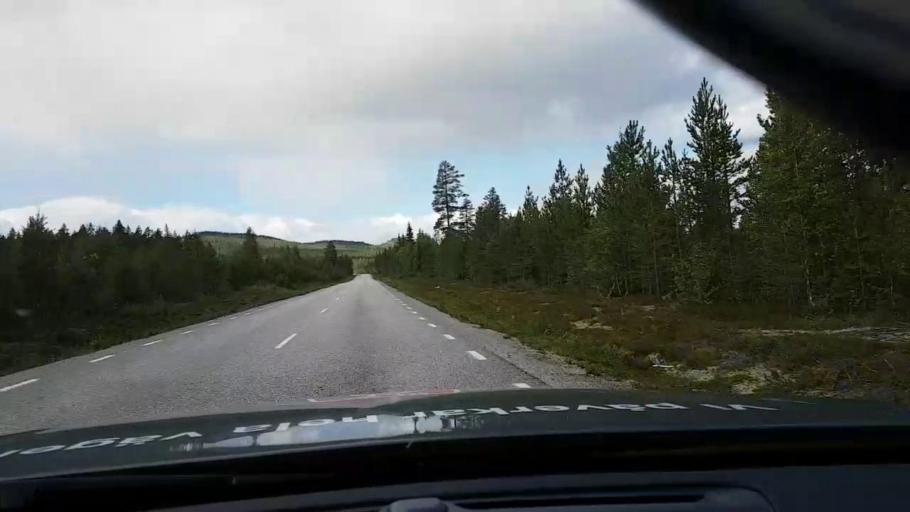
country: SE
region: Vaesternorrland
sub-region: OErnskoeldsviks Kommun
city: Bredbyn
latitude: 63.6804
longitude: 17.7853
